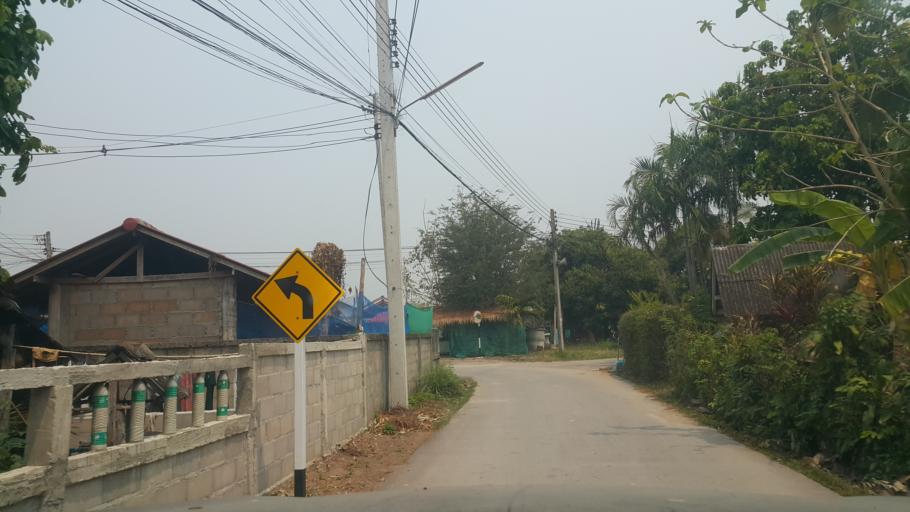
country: TH
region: Lampang
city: Hang Chat
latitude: 18.2726
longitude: 99.2545
